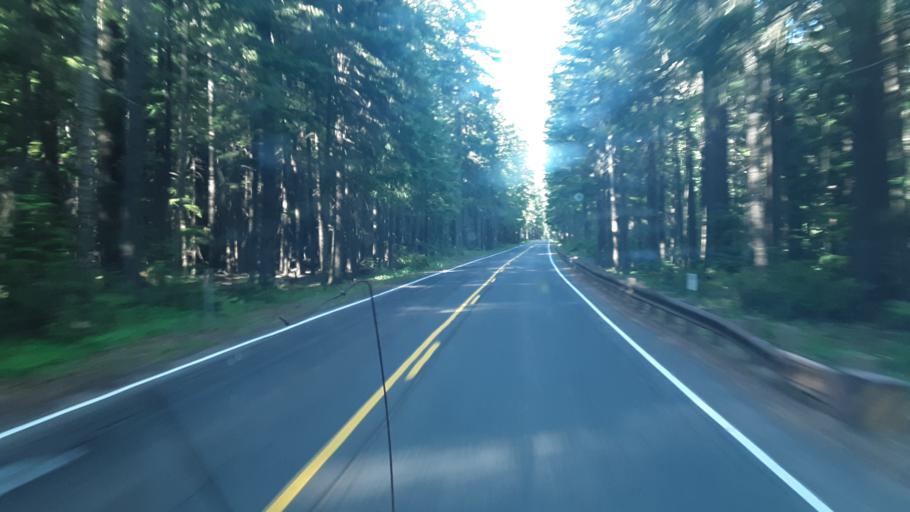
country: US
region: Oregon
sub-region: Jackson County
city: Shady Cove
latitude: 42.9480
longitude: -122.4113
